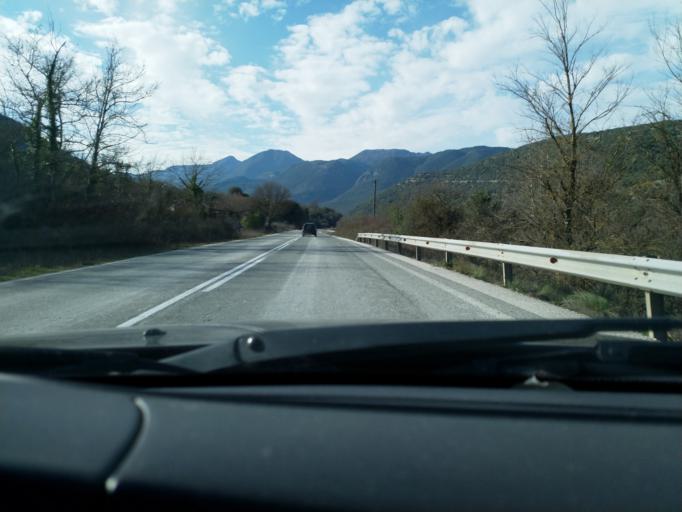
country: GR
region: Epirus
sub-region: Nomos Ioanninon
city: Agia Kyriaki
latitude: 39.4510
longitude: 20.8679
